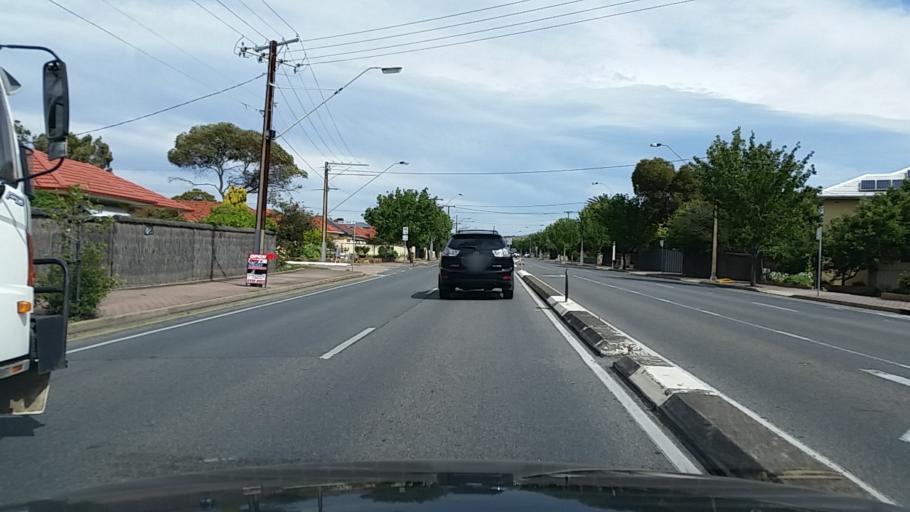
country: AU
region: South Australia
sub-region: Holdfast Bay
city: North Brighton
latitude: -34.9975
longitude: 138.5310
